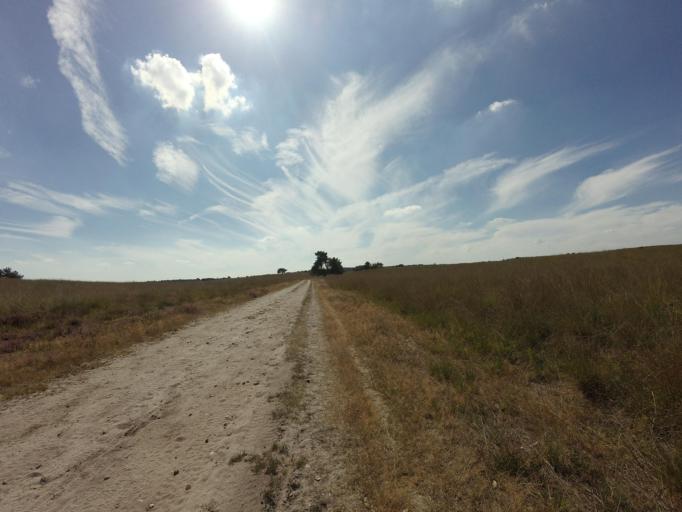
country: NL
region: Gelderland
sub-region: Gemeente Rheden
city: Rheden
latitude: 52.0535
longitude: 5.9975
